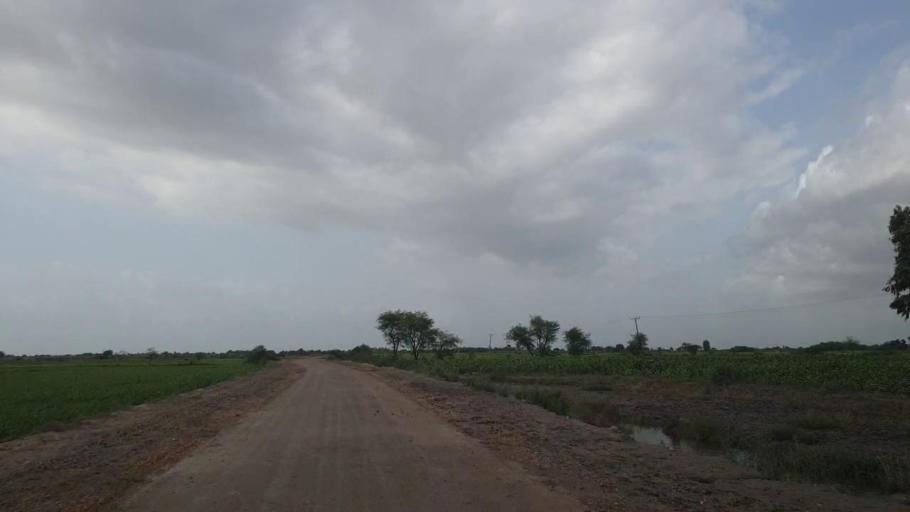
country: PK
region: Sindh
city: Kadhan
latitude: 24.5879
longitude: 69.0543
